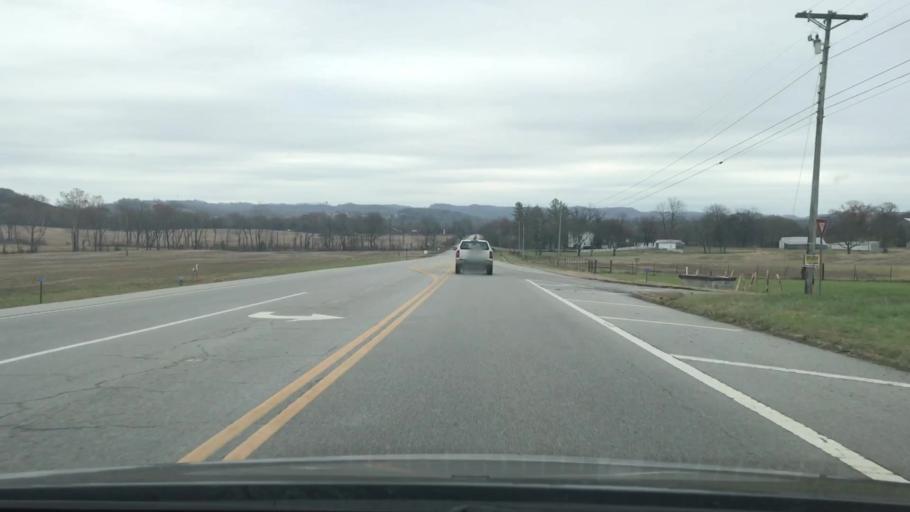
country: US
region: Tennessee
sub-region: Trousdale County
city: Hartsville
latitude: 36.3645
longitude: -86.0731
